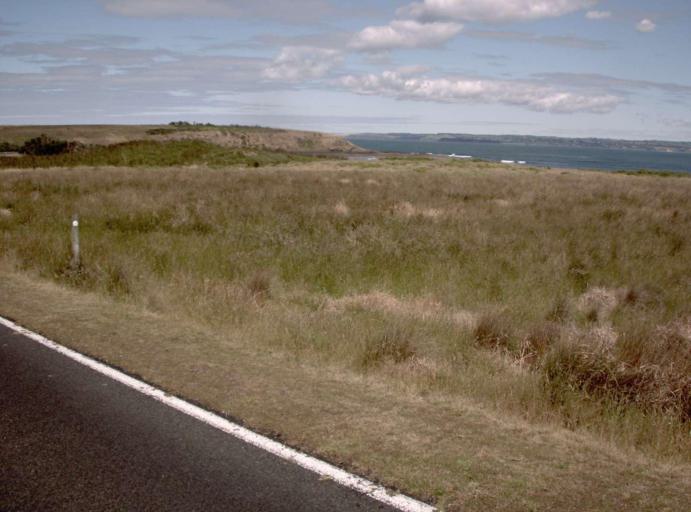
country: AU
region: Victoria
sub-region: Bass Coast
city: Phillip Island
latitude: -38.5067
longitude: 145.1403
